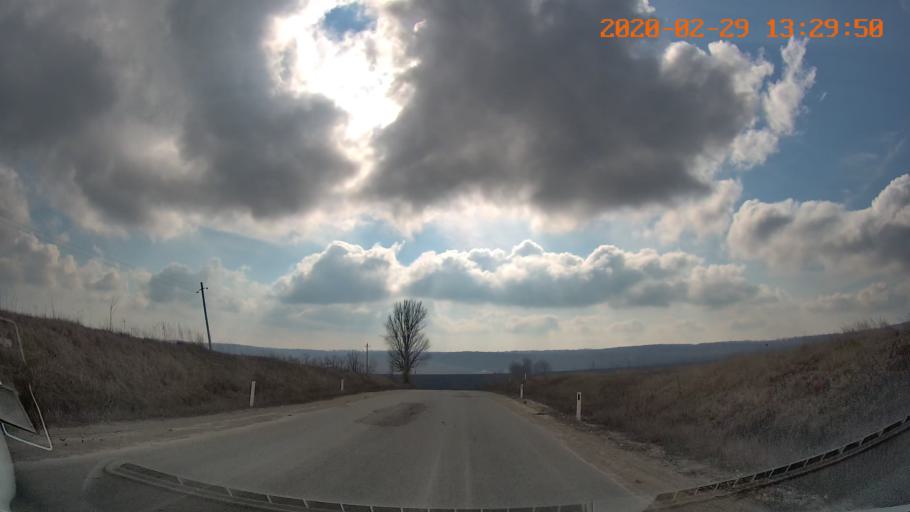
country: MD
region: Telenesti
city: Camenca
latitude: 47.8929
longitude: 28.6334
